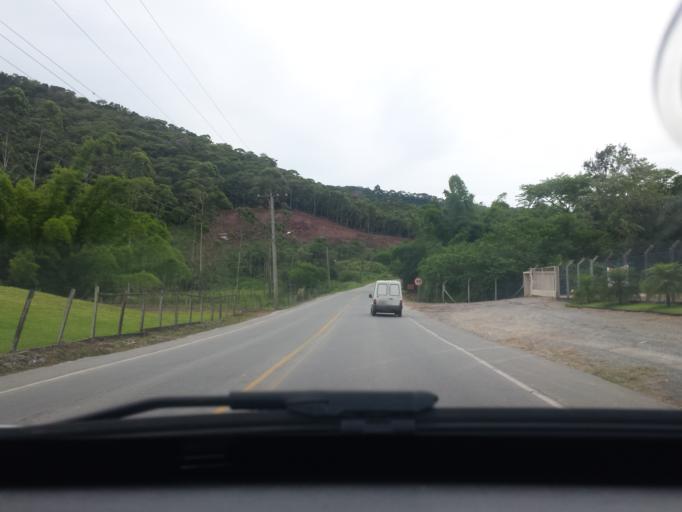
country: BR
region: Santa Catarina
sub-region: Gaspar
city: Gaspar
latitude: -26.8894
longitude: -48.9939
